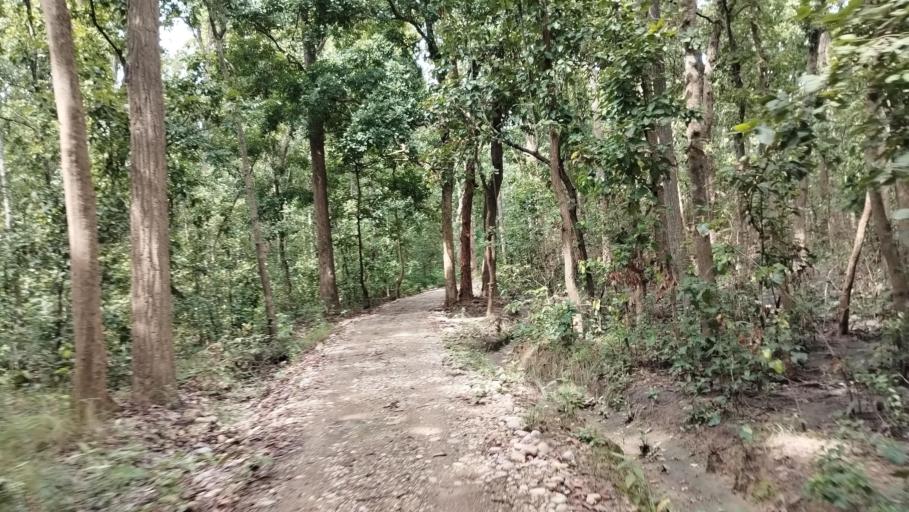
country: NP
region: Far Western
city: Tikapur
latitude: 28.4748
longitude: 81.2542
